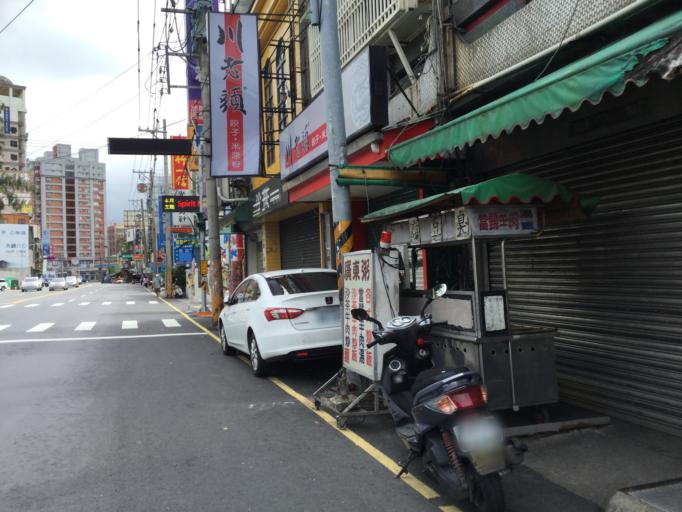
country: TW
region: Taiwan
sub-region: Hsinchu
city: Hsinchu
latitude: 24.7860
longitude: 121.0114
